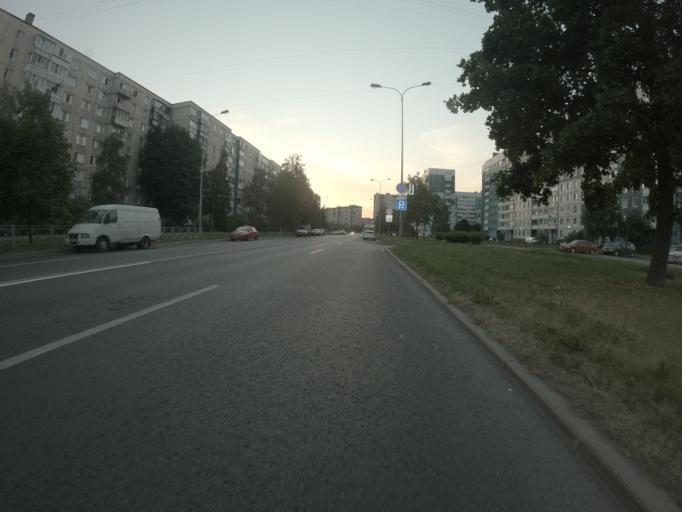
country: RU
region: St.-Petersburg
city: Krasnogvargeisky
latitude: 59.9144
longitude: 30.4588
